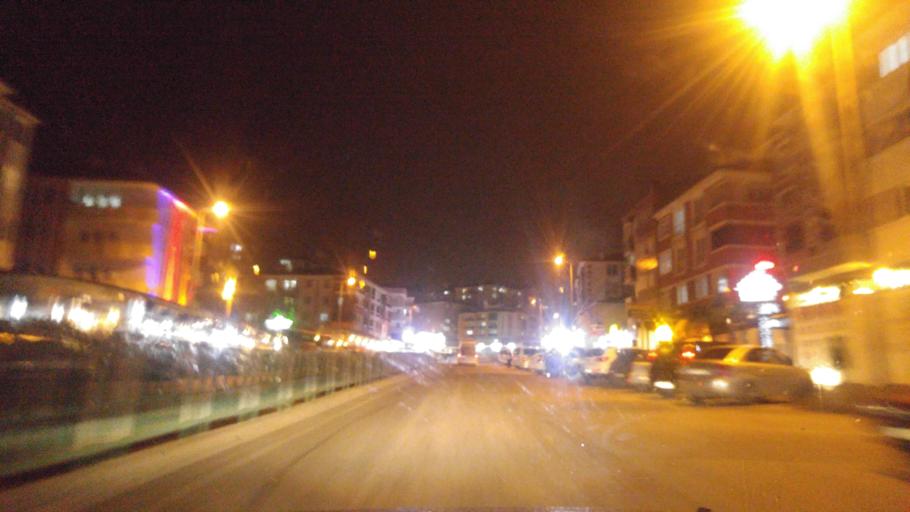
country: TR
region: Karabuk
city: Karabuk
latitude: 41.2191
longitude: 32.6603
